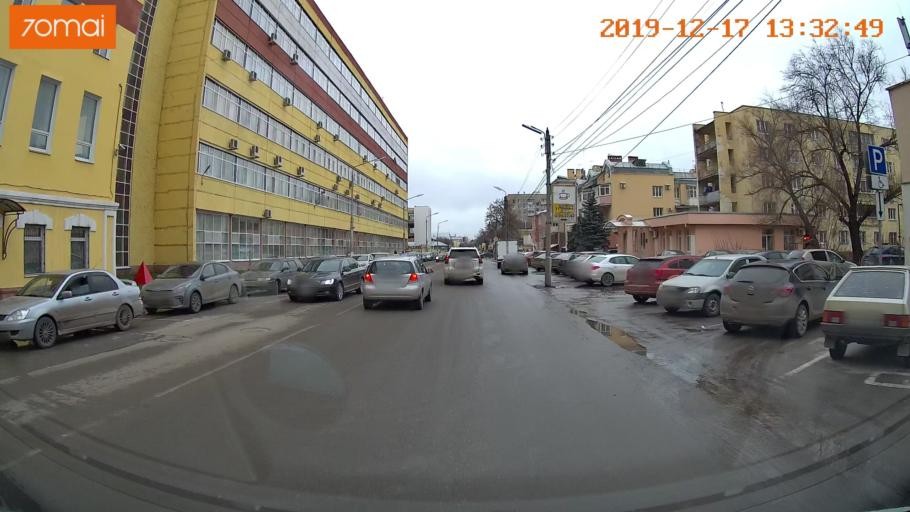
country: RU
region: Rjazan
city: Ryazan'
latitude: 54.6328
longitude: 39.7288
